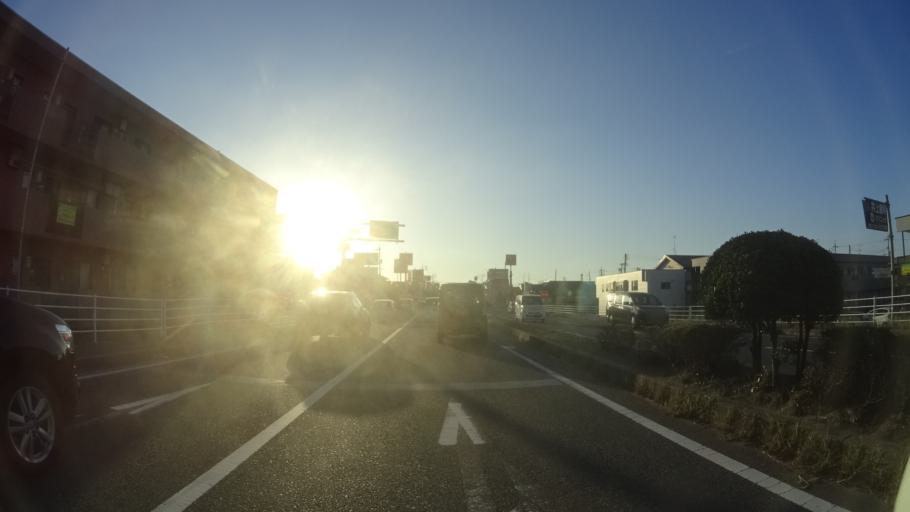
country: JP
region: Tottori
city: Yonago
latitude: 35.4492
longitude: 133.3667
